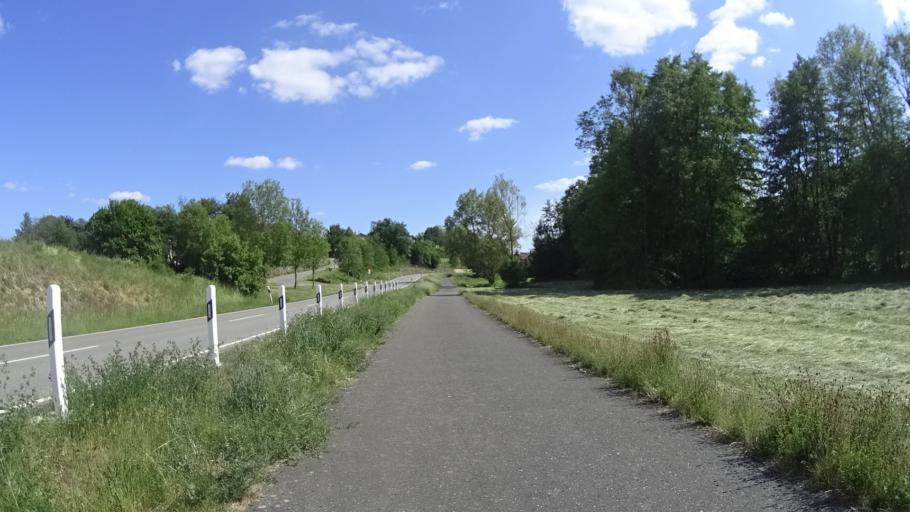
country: DE
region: Baden-Wuerttemberg
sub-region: Karlsruhe Region
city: Hardheim
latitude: 49.5583
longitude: 9.4959
